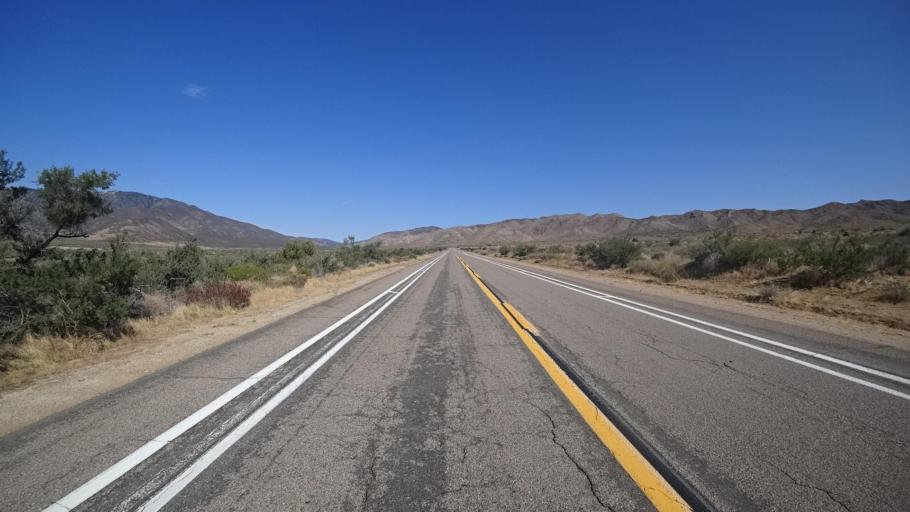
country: US
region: California
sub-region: San Diego County
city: Julian
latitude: 33.1164
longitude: -116.5130
